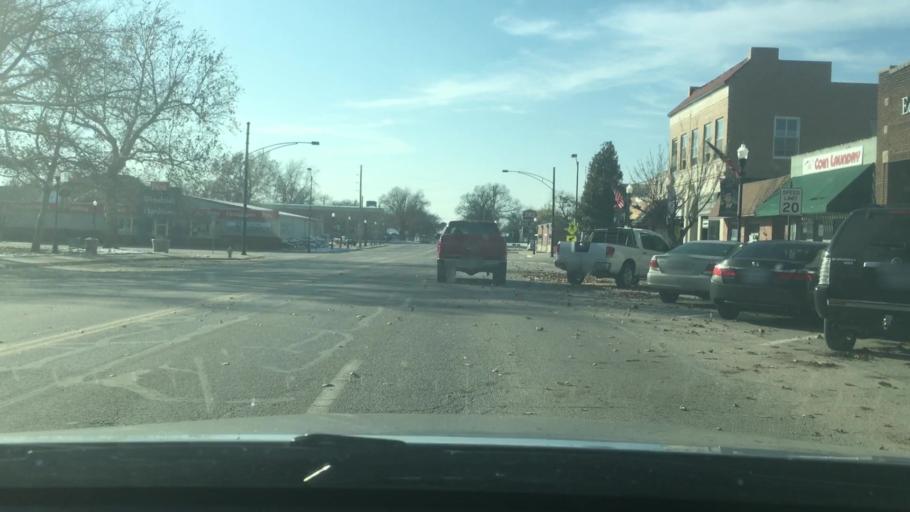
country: US
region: Kansas
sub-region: Rice County
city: Lyons
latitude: 38.3478
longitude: -98.2038
